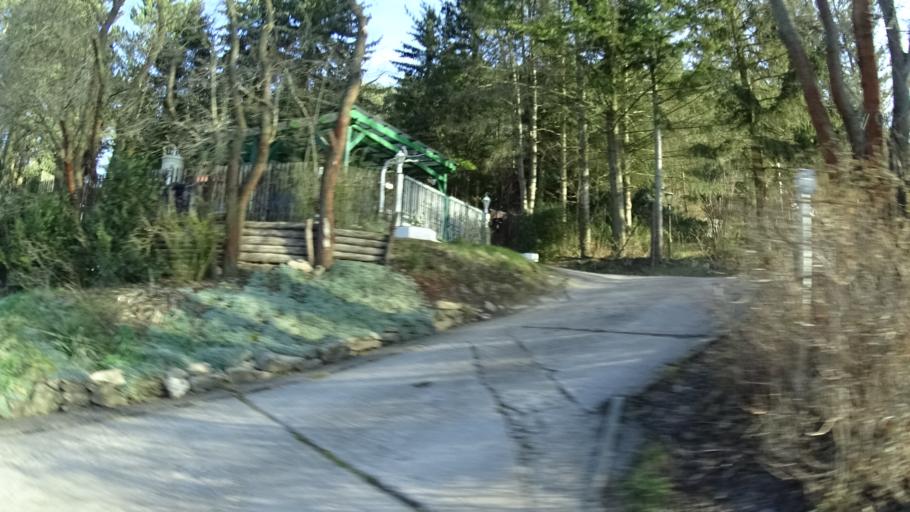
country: DE
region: Thuringia
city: Nauendorf
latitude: 50.8960
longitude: 11.1830
